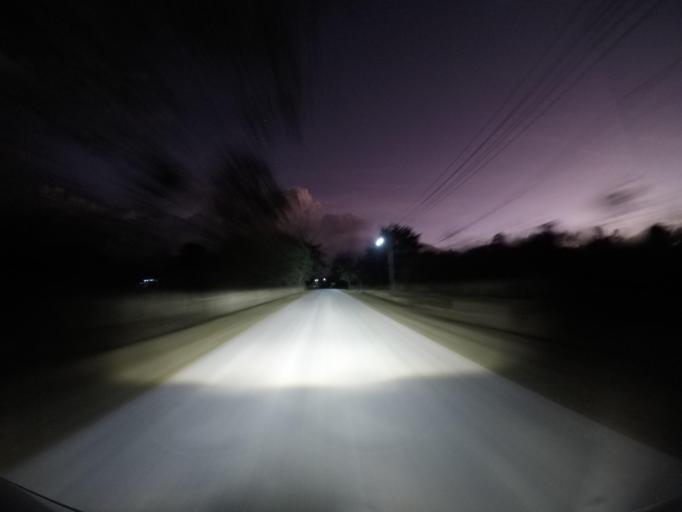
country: TL
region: Lautem
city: Lospalos
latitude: -8.4620
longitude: 126.9977
